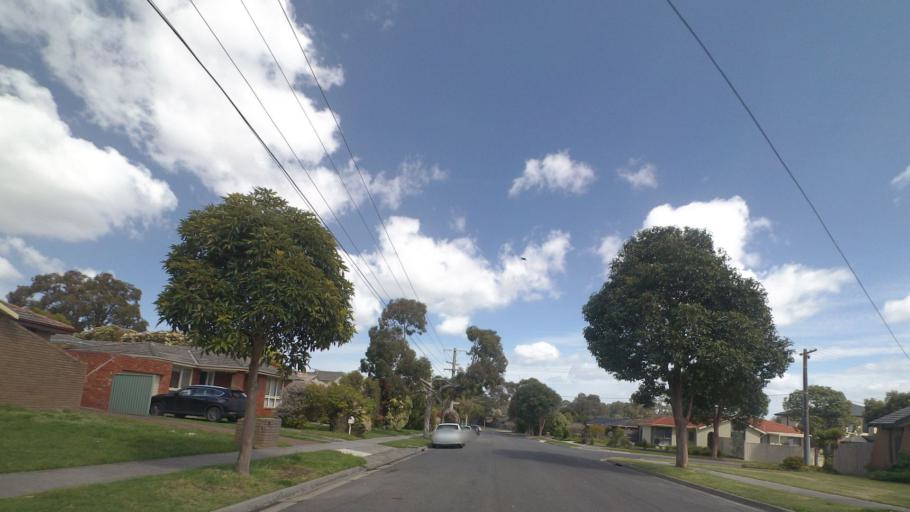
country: AU
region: Victoria
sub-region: Maroondah
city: Heathmont
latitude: -37.8439
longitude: 145.2368
